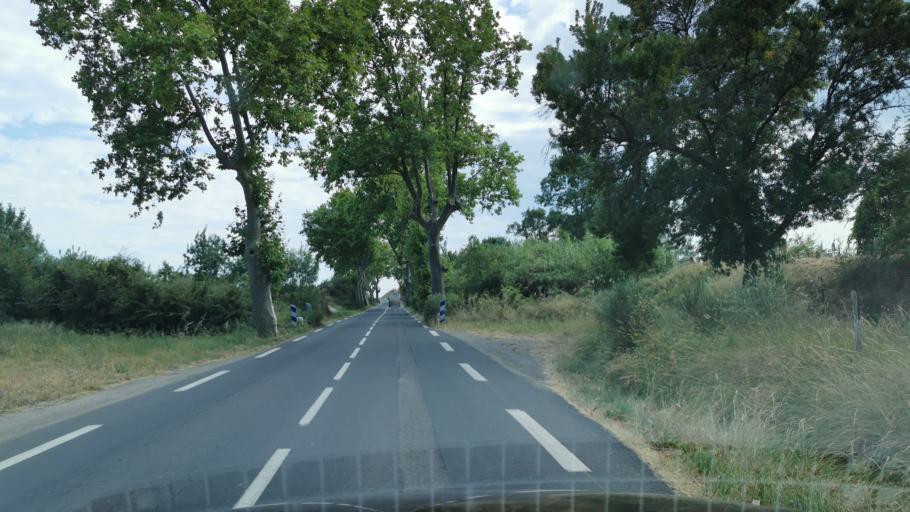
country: FR
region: Languedoc-Roussillon
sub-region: Departement de l'Herault
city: Puisserguier
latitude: 43.3593
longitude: 3.0393
